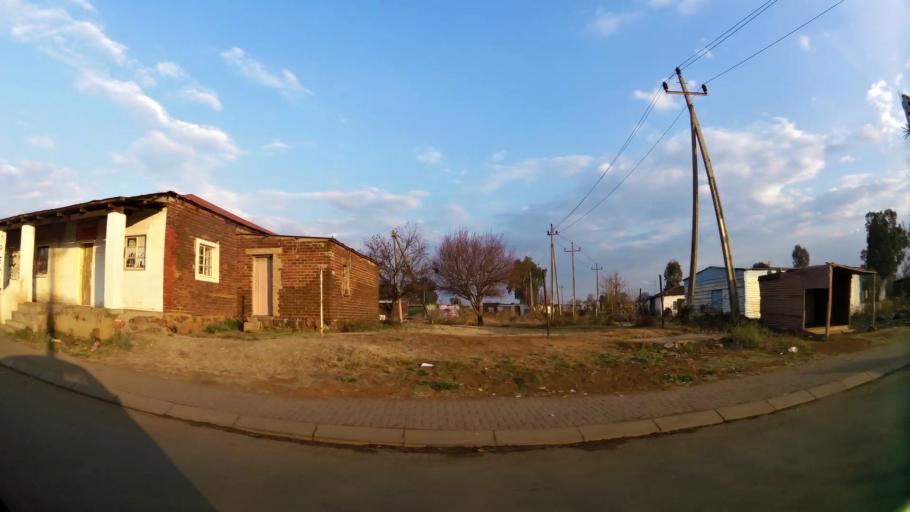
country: ZA
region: Gauteng
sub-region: City of Johannesburg Metropolitan Municipality
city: Orange Farm
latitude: -26.5344
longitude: 27.8482
